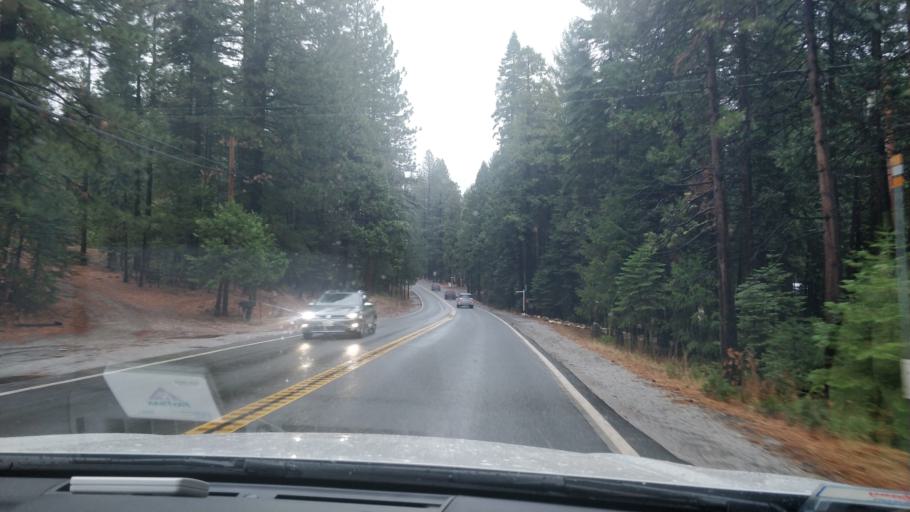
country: US
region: California
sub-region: Nevada County
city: Nevada City
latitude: 39.3174
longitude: -120.8913
